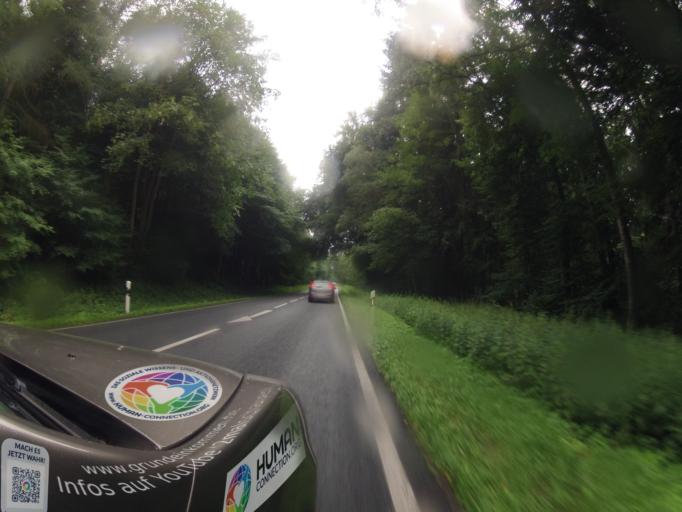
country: DE
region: Mecklenburg-Vorpommern
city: Usedom
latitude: 53.8864
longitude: 13.9471
